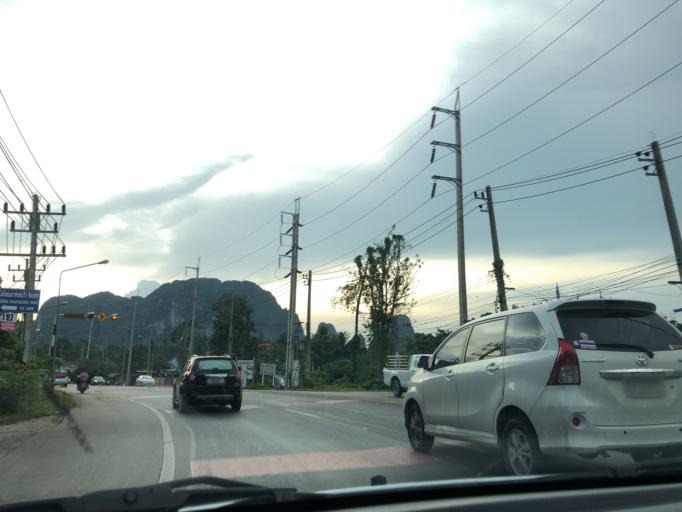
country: TH
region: Krabi
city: Krabi
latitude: 8.0829
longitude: 98.8680
